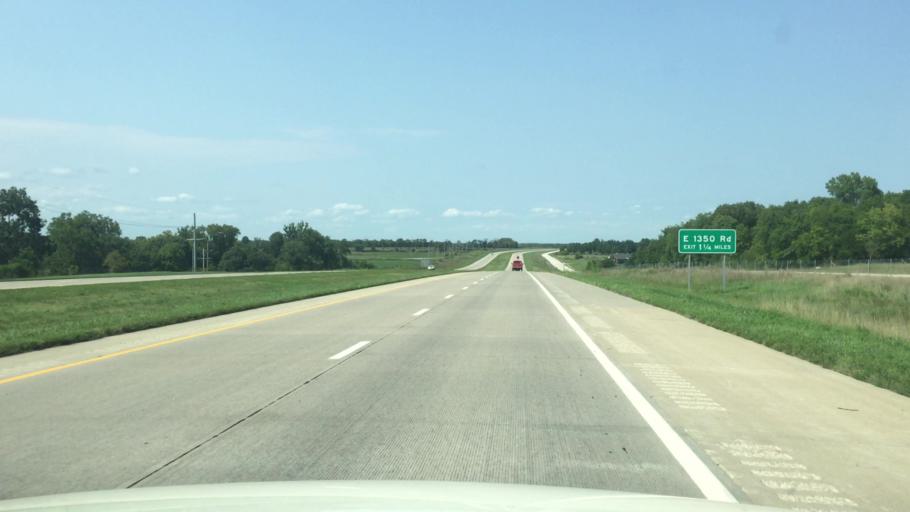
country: US
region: Kansas
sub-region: Linn County
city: Pleasanton
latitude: 38.1973
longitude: -94.7053
